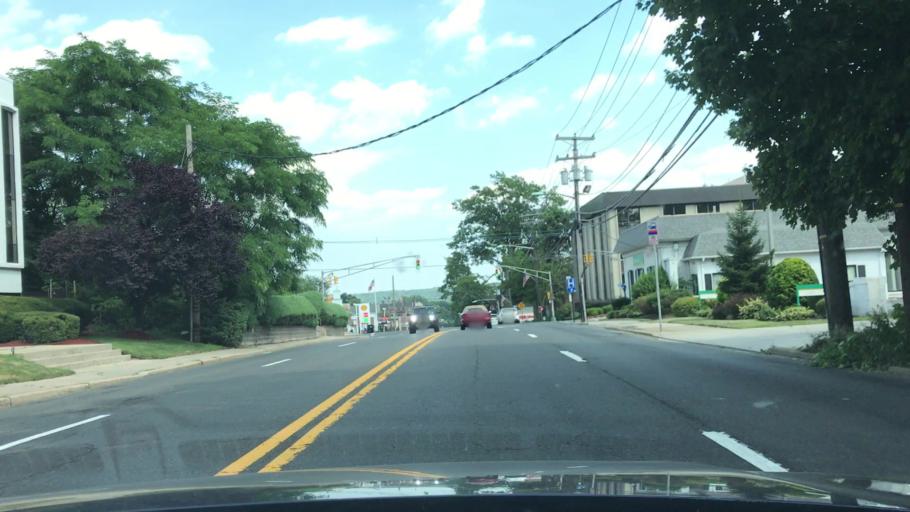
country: US
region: New Jersey
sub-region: Bergen County
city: Teaneck
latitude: 40.8870
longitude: -74.0158
